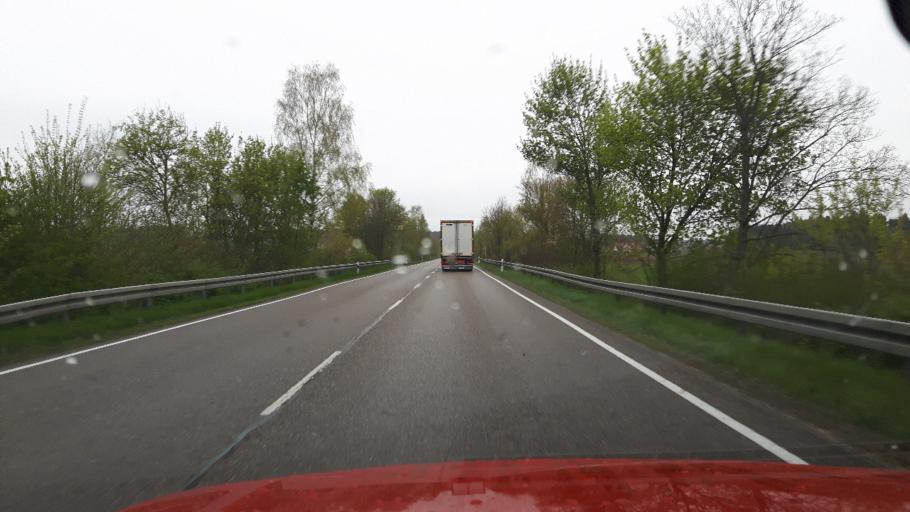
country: DE
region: Bavaria
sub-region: Regierungsbezirk Mittelfranken
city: Weidenbach
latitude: 49.2250
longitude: 10.6298
